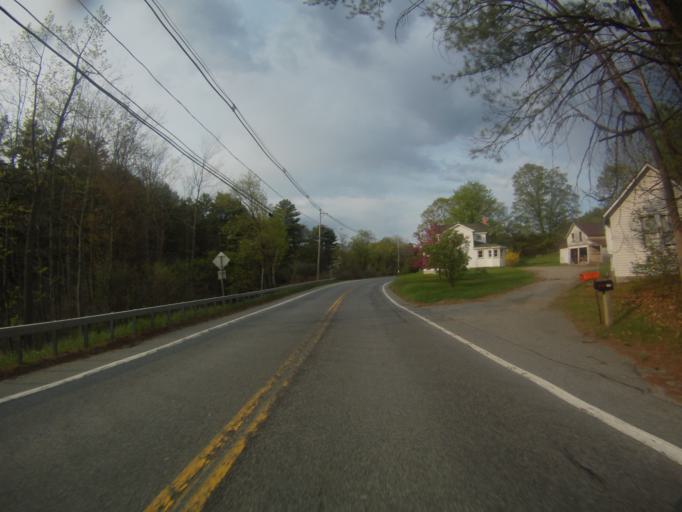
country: US
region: New York
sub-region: Warren County
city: Warrensburg
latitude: 43.6813
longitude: -73.7442
